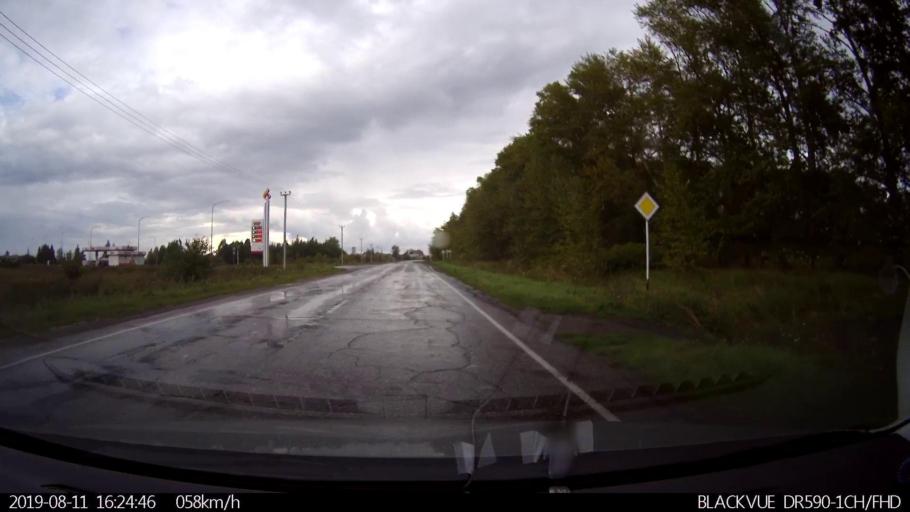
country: RU
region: Ulyanovsk
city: Mayna
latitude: 54.1026
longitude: 47.5980
